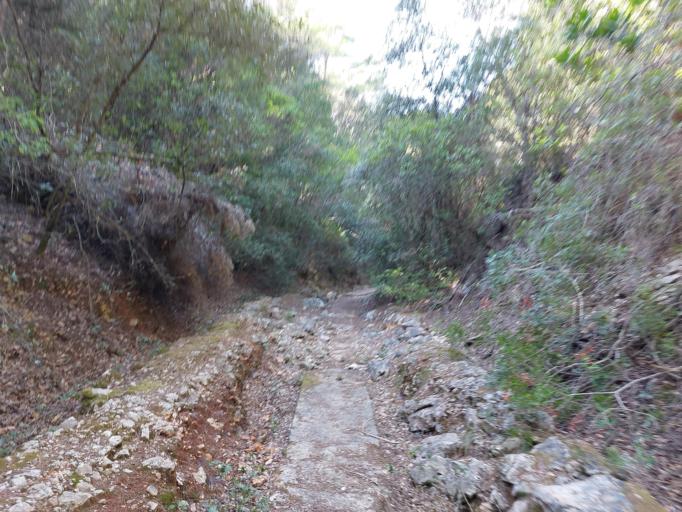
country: HR
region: Dubrovacko-Neretvanska
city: Smokvica
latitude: 42.7397
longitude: 16.8253
